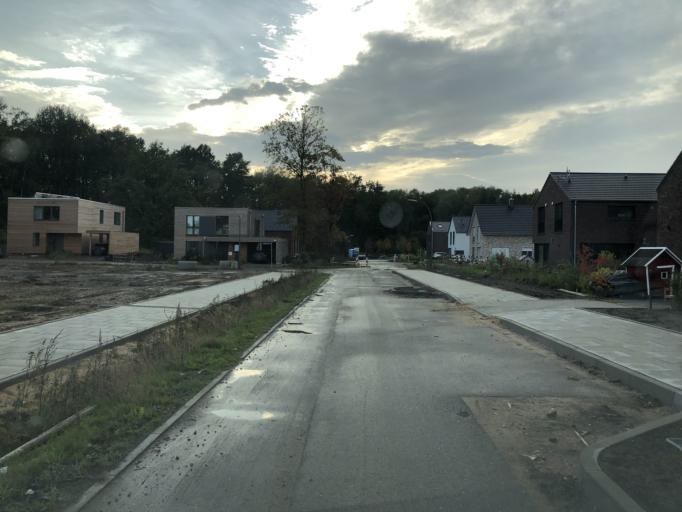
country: DE
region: Lower Saxony
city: Neu Wulmstorf
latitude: 53.4639
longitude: 9.8116
